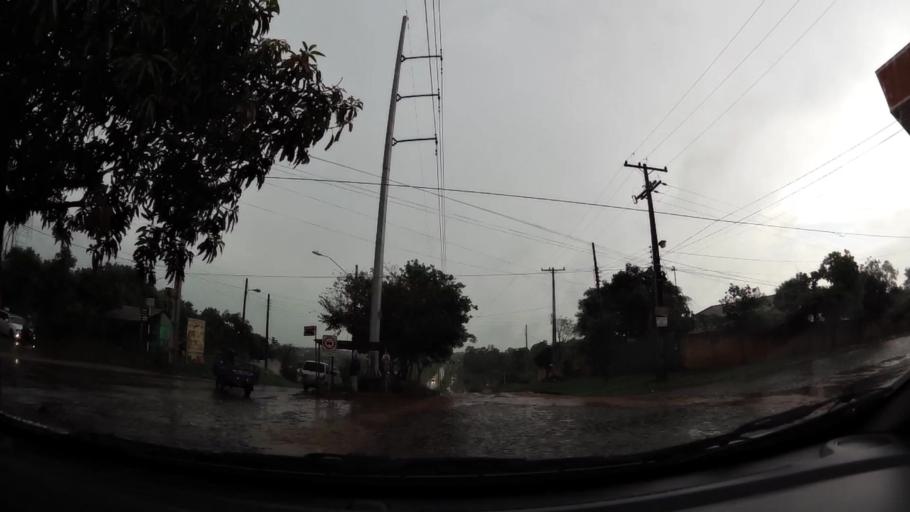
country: PY
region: Alto Parana
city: Presidente Franco
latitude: -25.5212
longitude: -54.6759
